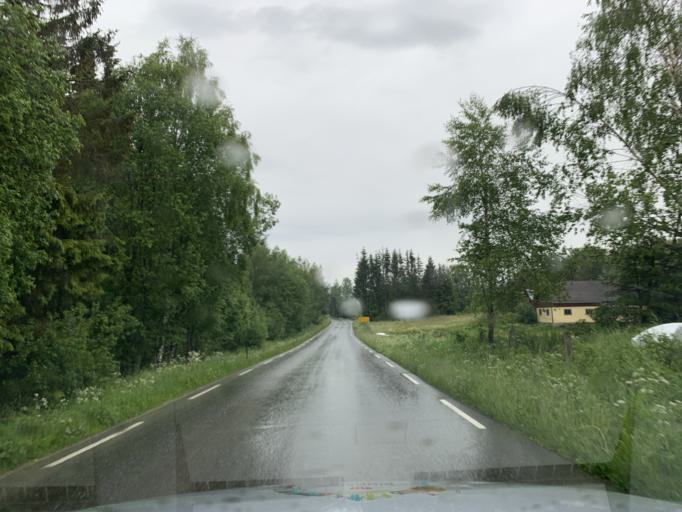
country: NO
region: Oppland
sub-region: Ringebu
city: Ringebu
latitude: 61.4462
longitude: 10.1803
